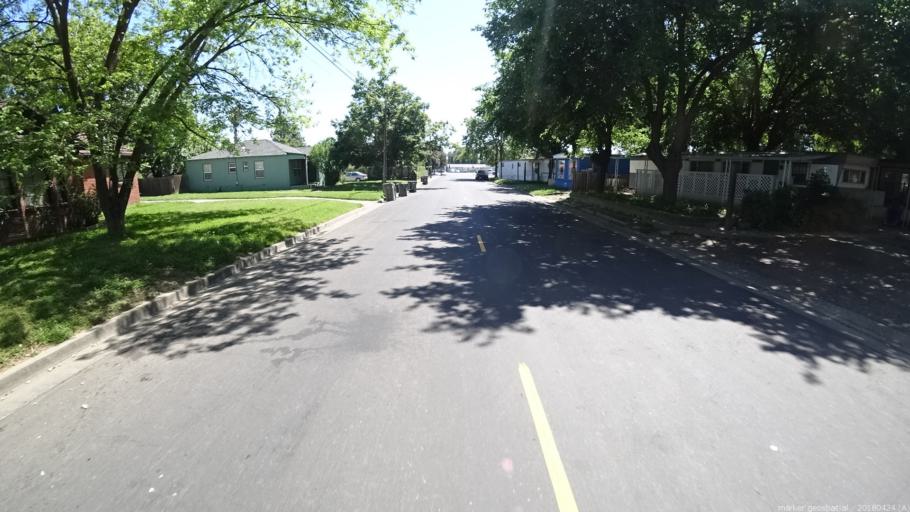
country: US
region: California
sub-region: Yolo County
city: West Sacramento
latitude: 38.5809
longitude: -121.5420
